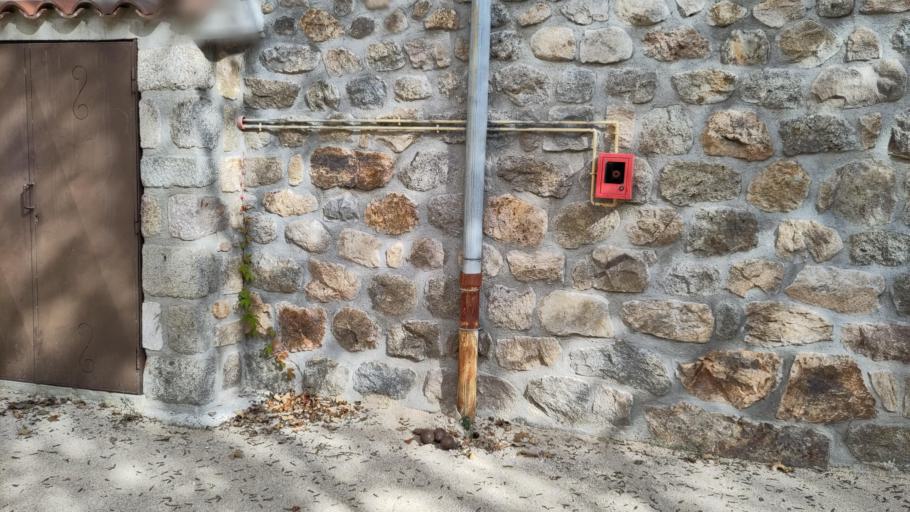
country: FR
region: Rhone-Alpes
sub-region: Departement de l'Ardeche
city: Le Cheylard
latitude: 44.8216
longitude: 4.4288
